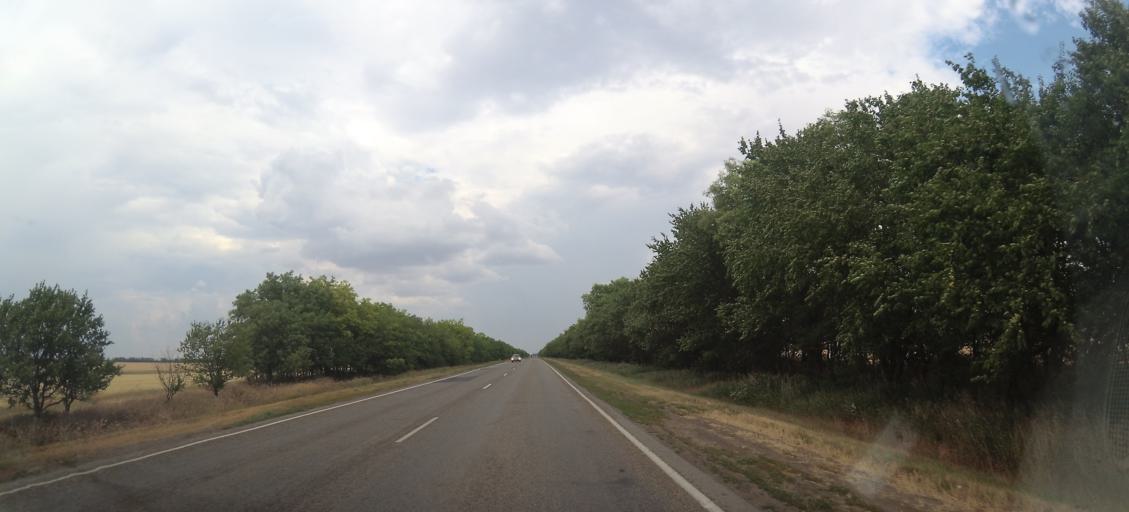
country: RU
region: Rostov
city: Gigant
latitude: 46.3349
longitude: 41.3947
